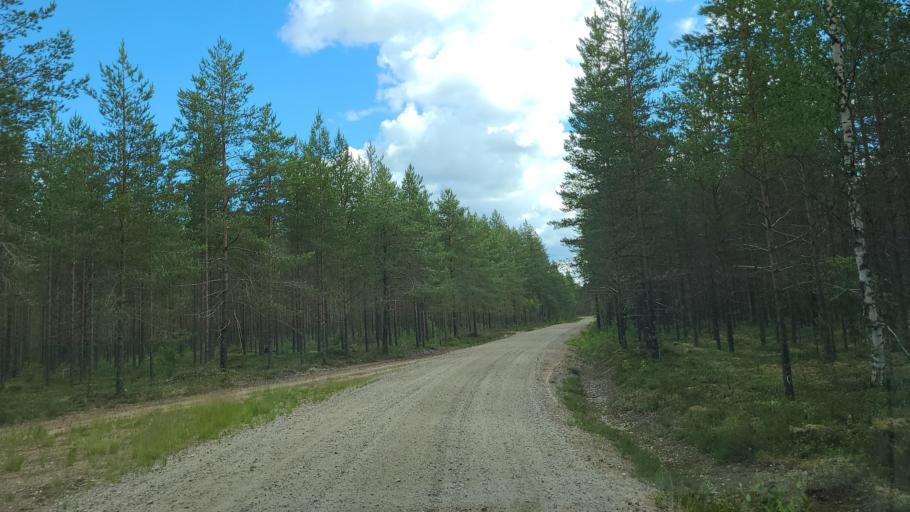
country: FI
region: Northern Savo
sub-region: Koillis-Savo
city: Kaavi
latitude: 63.0517
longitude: 28.8148
